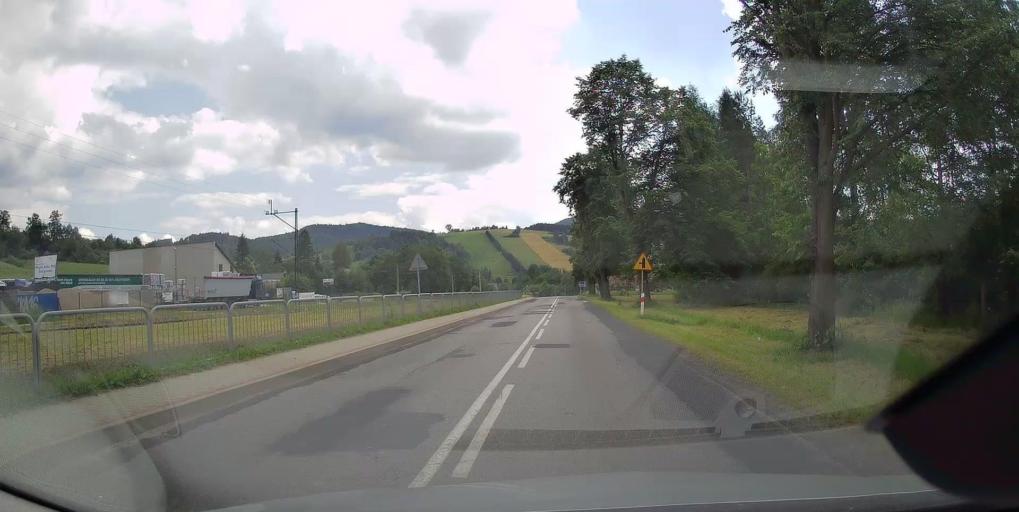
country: PL
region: Lesser Poland Voivodeship
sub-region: Powiat nowosadecki
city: Krynica-Zdroj
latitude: 49.3757
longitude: 20.9504
